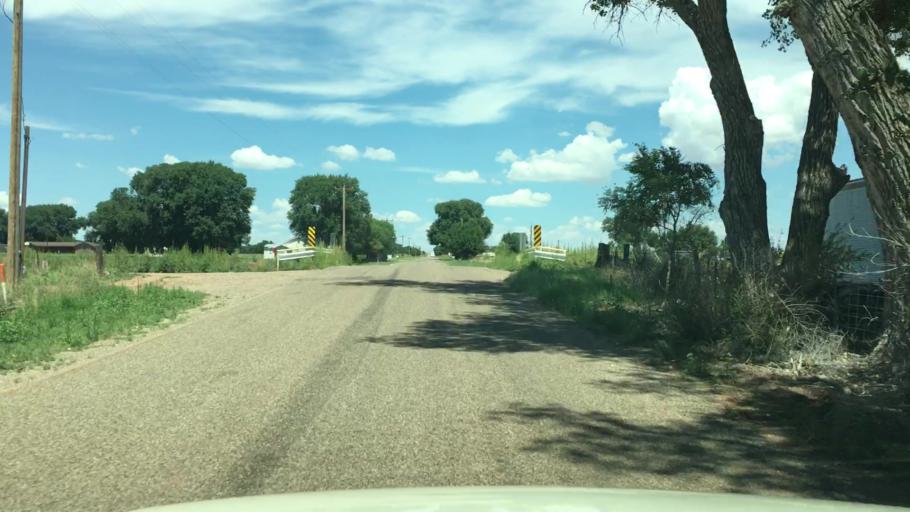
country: US
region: New Mexico
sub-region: De Baca County
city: Fort Sumner
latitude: 34.4395
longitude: -104.1936
